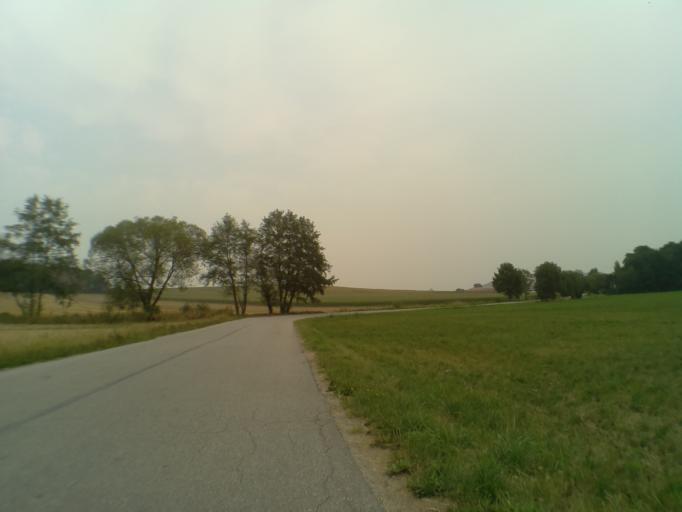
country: PL
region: Lower Silesian Voivodeship
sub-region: Powiat swidnicki
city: Strzegom
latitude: 50.9820
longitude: 16.3157
